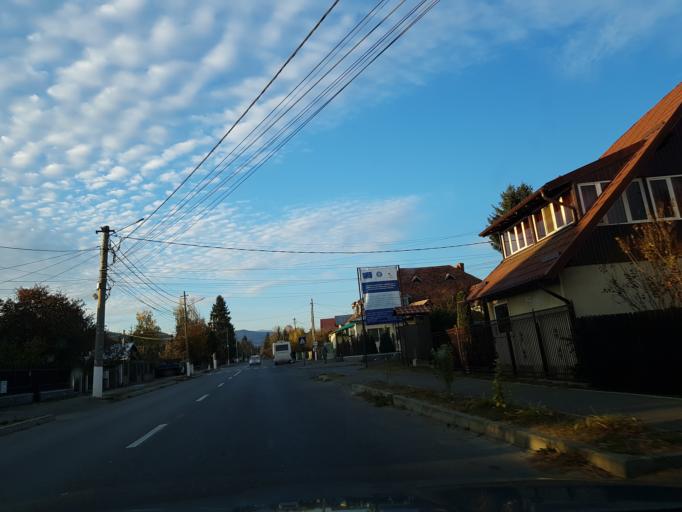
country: RO
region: Prahova
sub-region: Oras Breaza
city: Breaza
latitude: 45.1884
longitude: 25.6610
